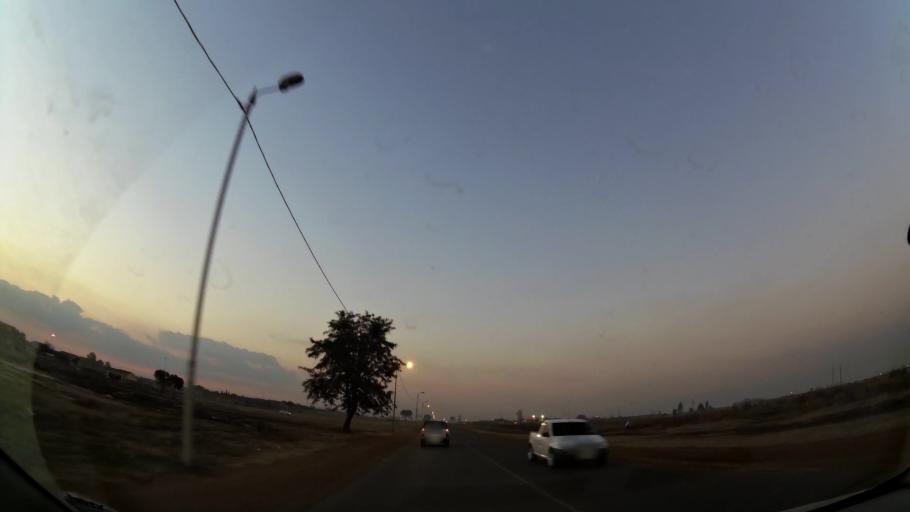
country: ZA
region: Gauteng
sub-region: Ekurhuleni Metropolitan Municipality
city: Springs
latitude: -26.3445
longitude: 28.3701
